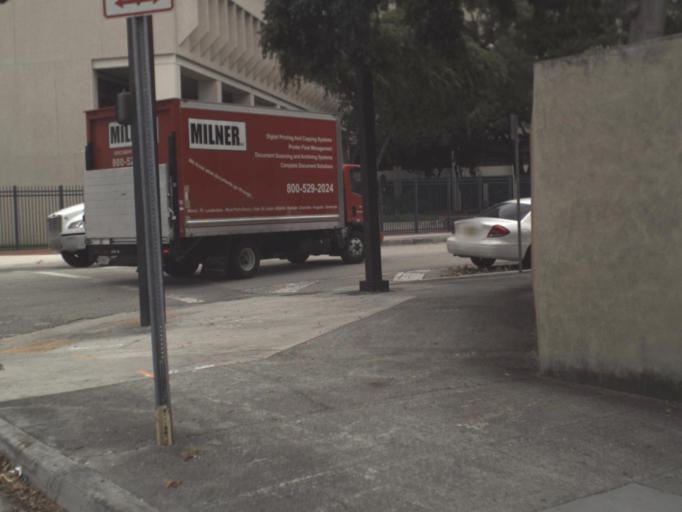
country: US
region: Florida
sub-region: Miami-Dade County
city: Miami
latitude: 25.7788
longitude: -80.1981
